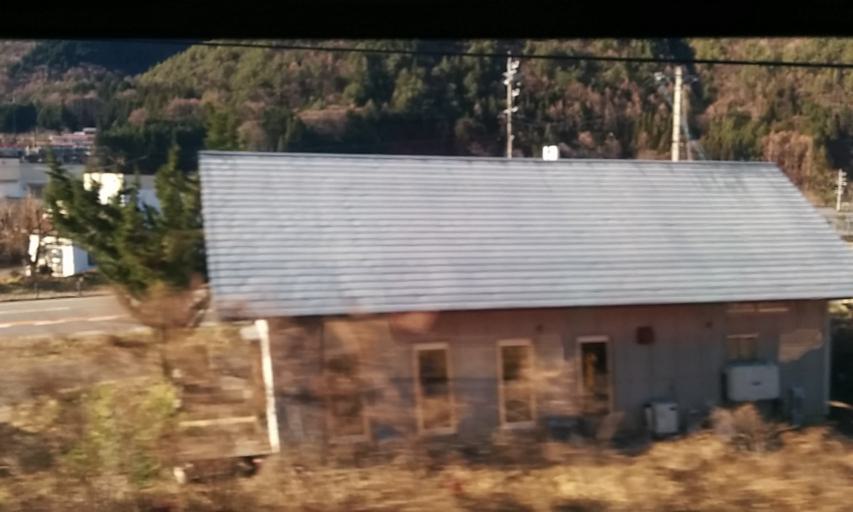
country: JP
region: Nagano
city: Ina
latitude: 35.8596
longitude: 137.7213
